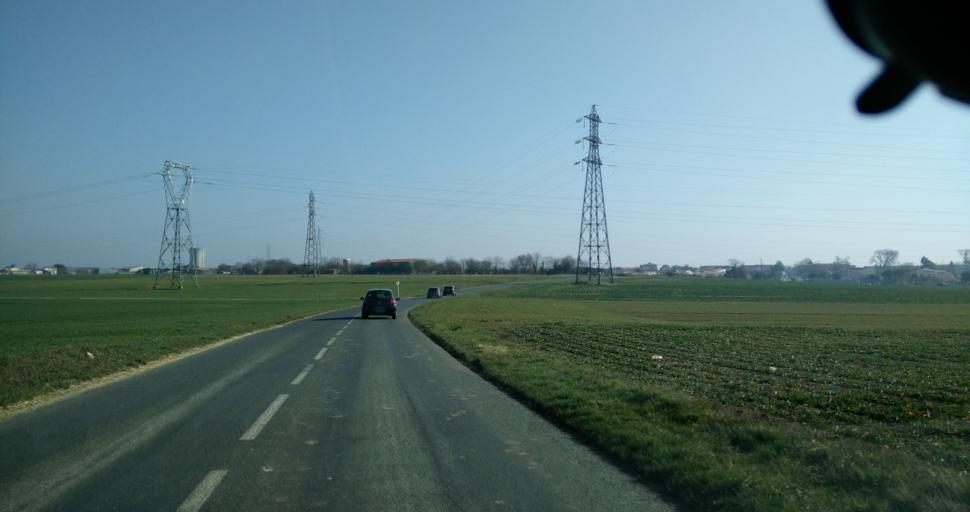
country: FR
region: Poitou-Charentes
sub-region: Departement de la Charente-Maritime
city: Puilboreau
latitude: 46.1895
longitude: -1.1271
